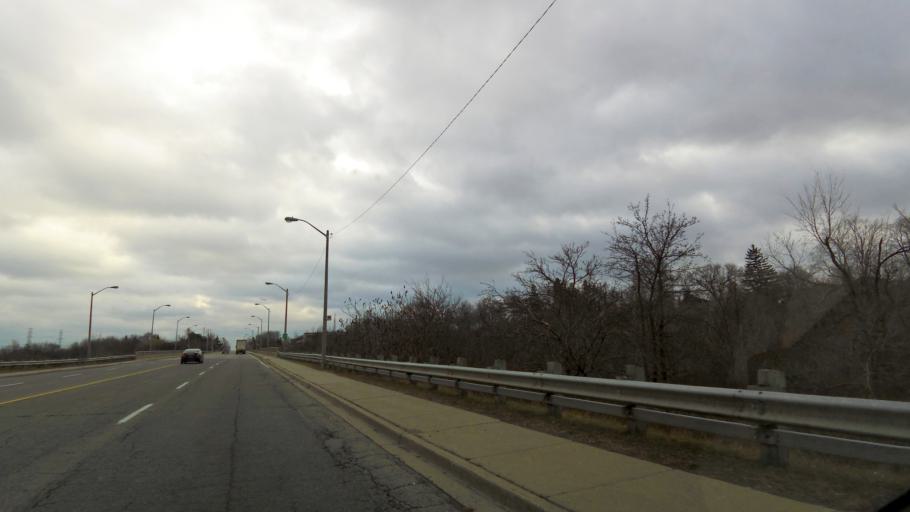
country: CA
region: Ontario
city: Etobicoke
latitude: 43.7310
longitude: -79.5626
